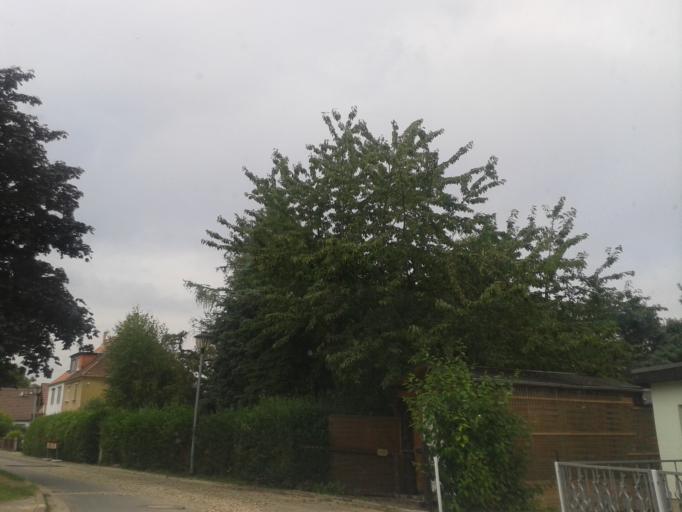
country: DE
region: Saxony
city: Freital
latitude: 51.0319
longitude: 13.6642
